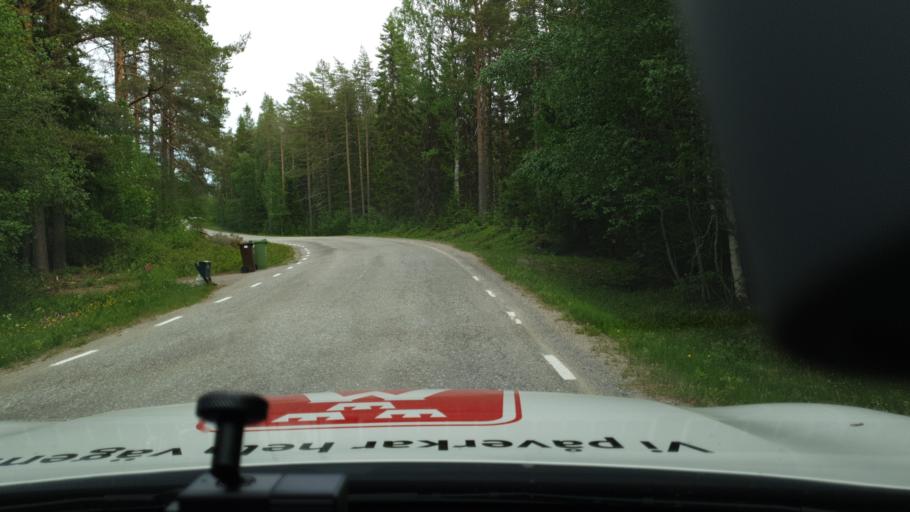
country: SE
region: Vaesterbotten
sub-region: Umea Kommun
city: Hoernefors
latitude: 63.5658
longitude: 19.7959
